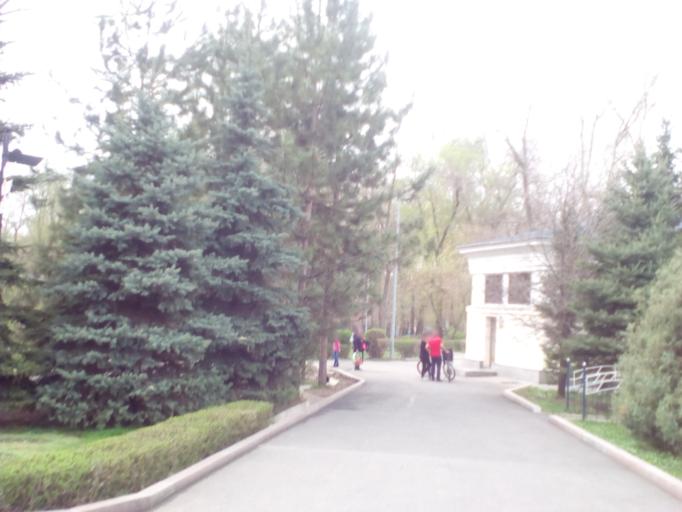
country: KZ
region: Almaty Qalasy
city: Almaty
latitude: 43.2621
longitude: 76.9699
